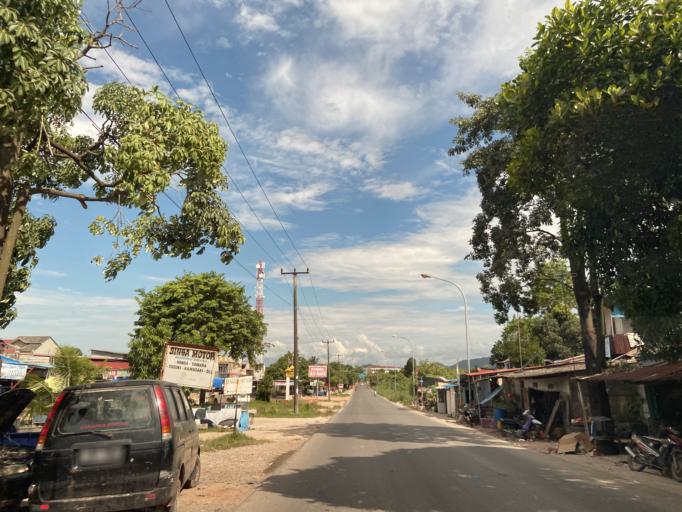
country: SG
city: Singapore
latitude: 1.0395
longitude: 103.9374
